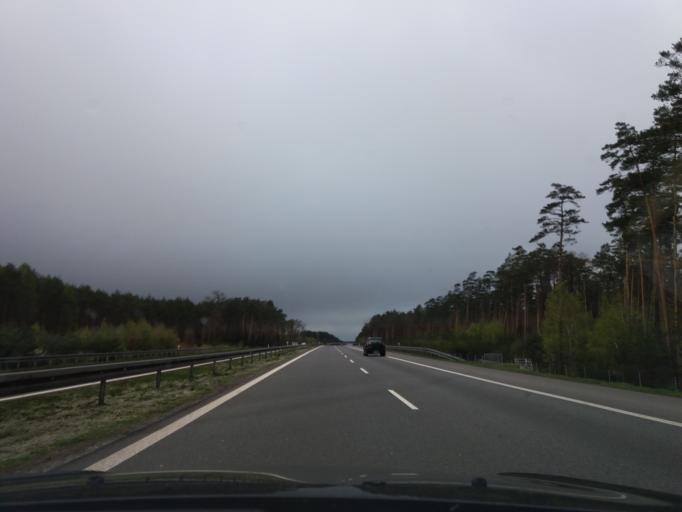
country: PL
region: Opole Voivodeship
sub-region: Powiat opolski
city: Komprachcice
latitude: 50.5942
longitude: 17.8033
